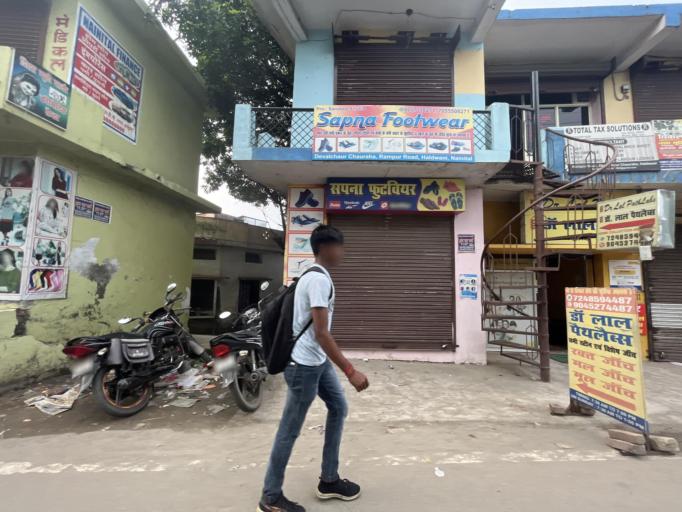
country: IN
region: Uttarakhand
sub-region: Naini Tal
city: Haldwani
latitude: 29.1941
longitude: 79.5082
